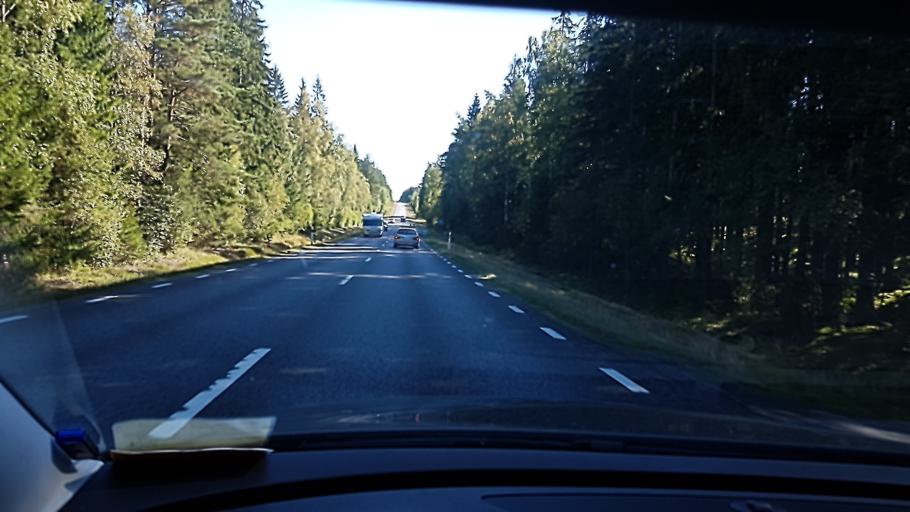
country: SE
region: Kronoberg
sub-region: Lessebo Kommun
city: Lessebo
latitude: 56.7322
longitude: 15.4188
